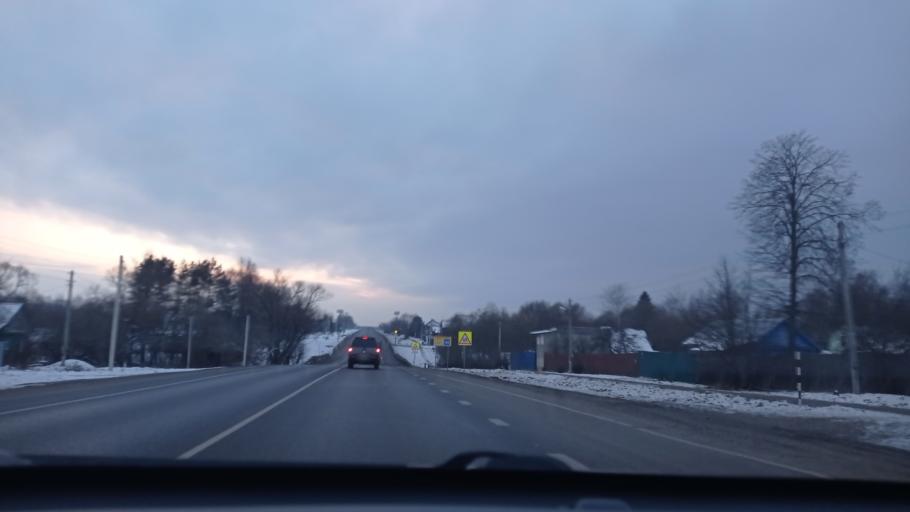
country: RU
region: Moskovskaya
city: Ateptsevo
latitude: 55.1983
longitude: 36.9198
